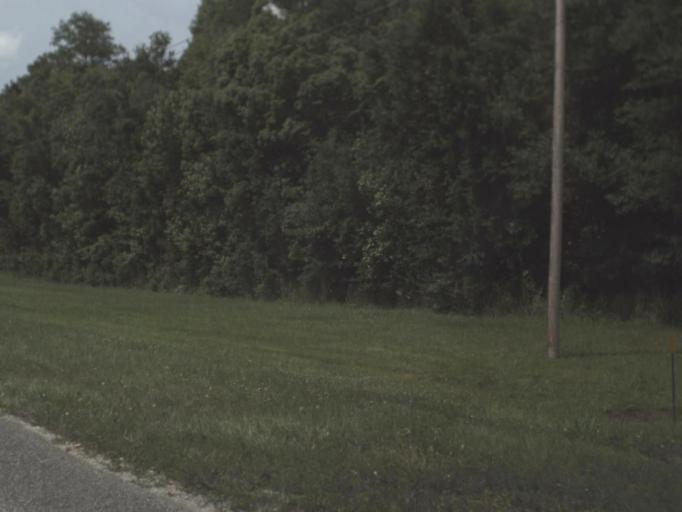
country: US
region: Florida
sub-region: Clay County
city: Green Cove Springs
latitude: 29.9667
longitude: -81.6738
